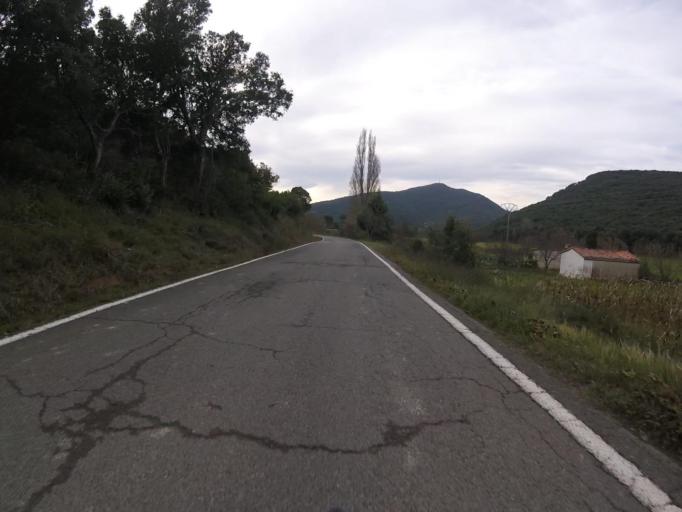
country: ES
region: Navarre
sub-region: Provincia de Navarra
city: Estella
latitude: 42.7051
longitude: -2.0522
